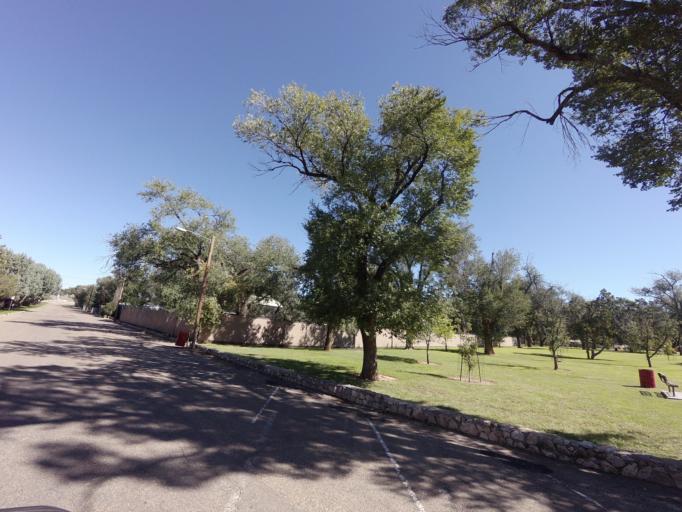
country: US
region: New Mexico
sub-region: Curry County
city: Clovis
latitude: 34.4086
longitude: -103.1875
